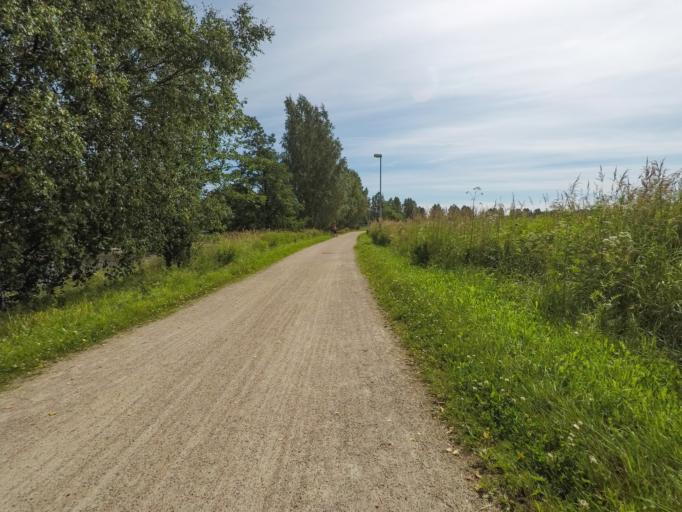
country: FI
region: Uusimaa
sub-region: Helsinki
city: Vantaa
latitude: 60.2544
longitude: 24.9774
